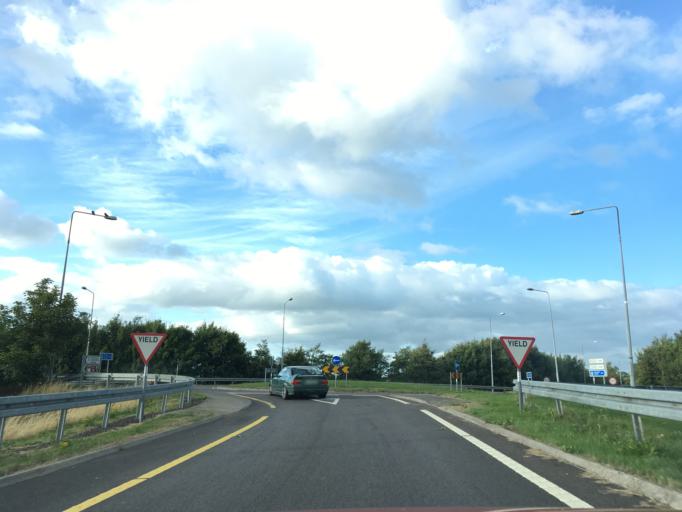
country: IE
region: Munster
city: Cashel
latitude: 52.5085
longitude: -7.8722
